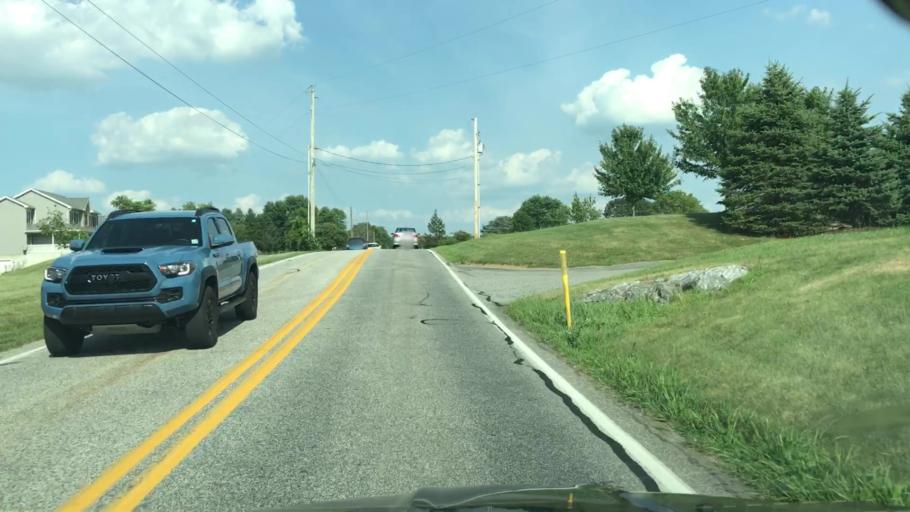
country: US
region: Pennsylvania
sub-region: Cumberland County
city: Boiling Springs
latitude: 40.1815
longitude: -77.0999
